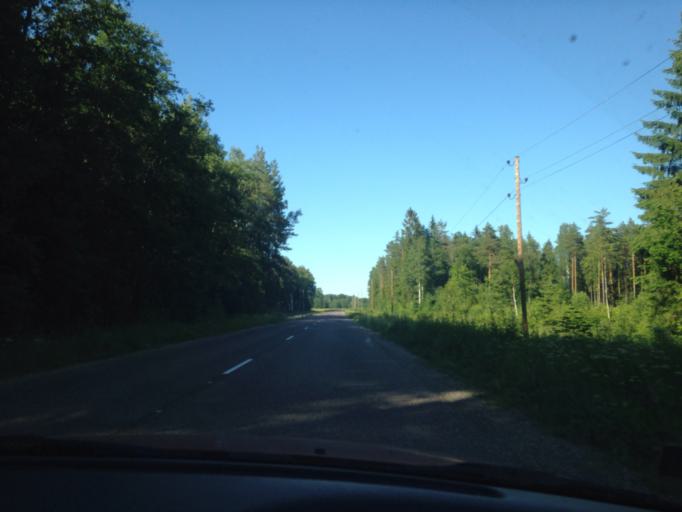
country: LV
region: Saulkrastu
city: Saulkrasti
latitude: 57.2468
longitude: 24.4939
